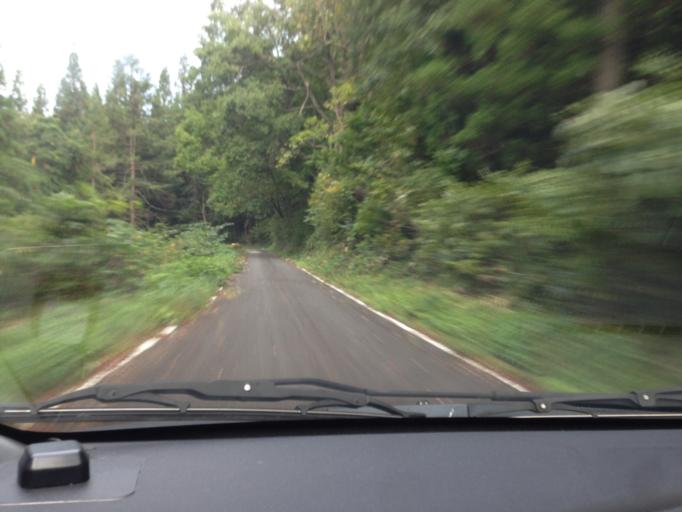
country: JP
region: Fukushima
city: Kitakata
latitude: 37.3538
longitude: 139.6009
